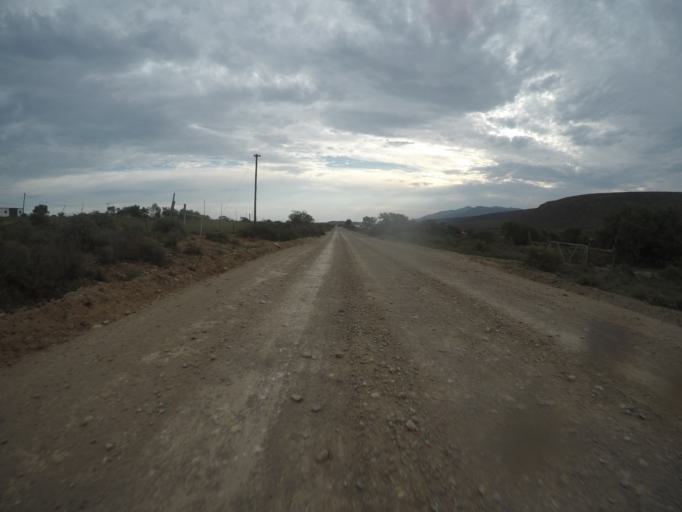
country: ZA
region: Eastern Cape
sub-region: Cacadu District Municipality
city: Willowmore
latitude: -33.4915
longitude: 23.5963
